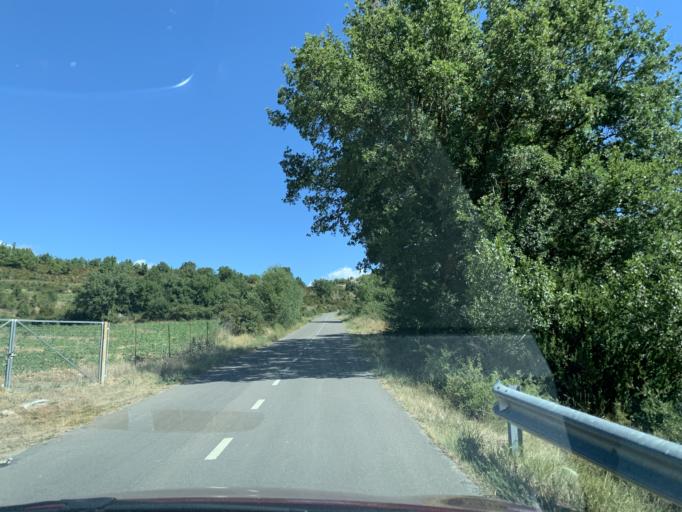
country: ES
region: Aragon
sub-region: Provincia de Huesca
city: Sabinanigo
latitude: 42.5418
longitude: -0.3178
